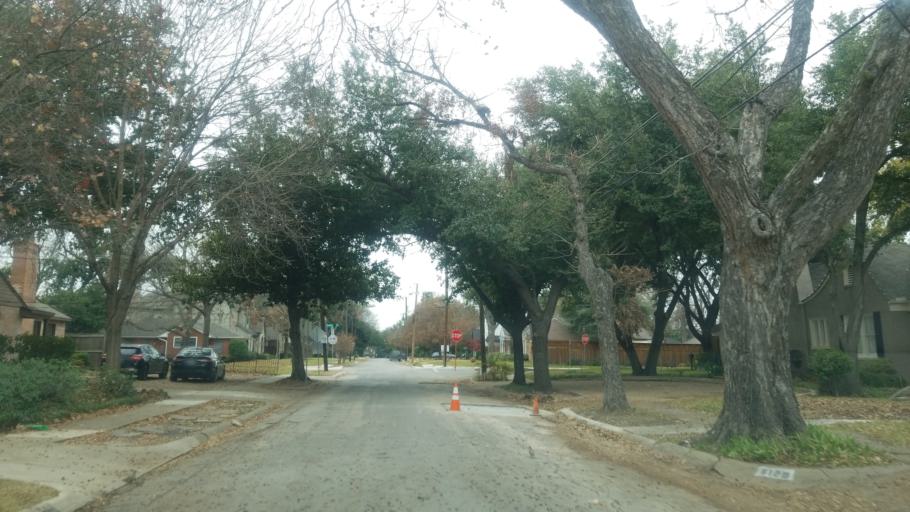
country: US
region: Texas
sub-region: Dallas County
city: Highland Park
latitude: 32.8203
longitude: -96.8256
